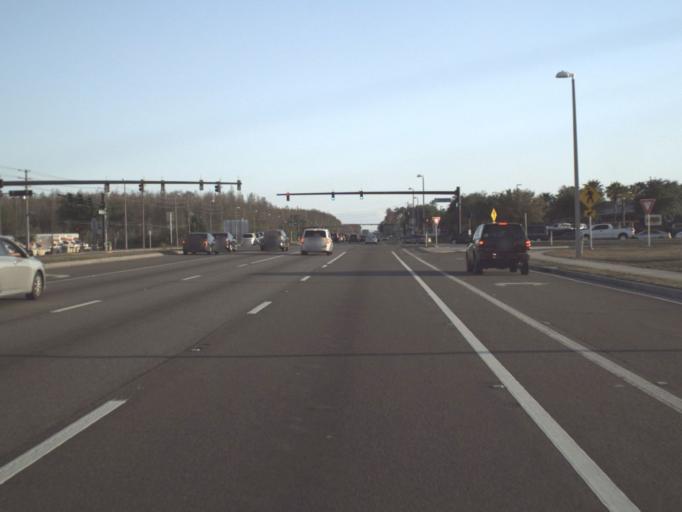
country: US
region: Florida
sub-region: Orange County
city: Hunters Creek
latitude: 28.3724
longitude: -81.4046
